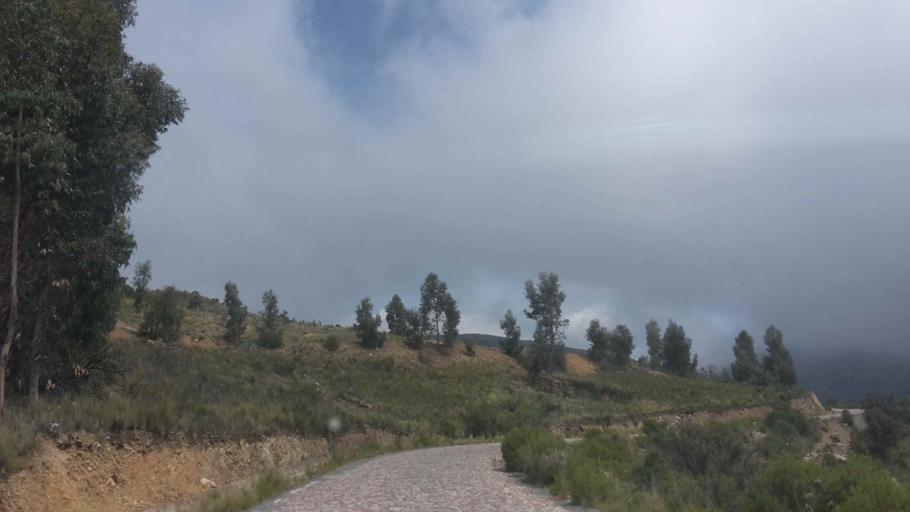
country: BO
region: Cochabamba
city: Cochabamba
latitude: -17.3347
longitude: -66.0688
